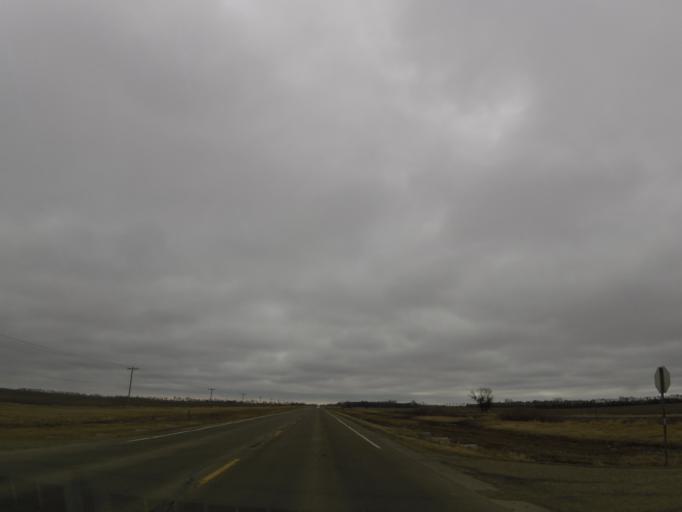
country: US
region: North Dakota
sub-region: Traill County
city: Hillsboro
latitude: 47.1810
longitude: -97.2175
